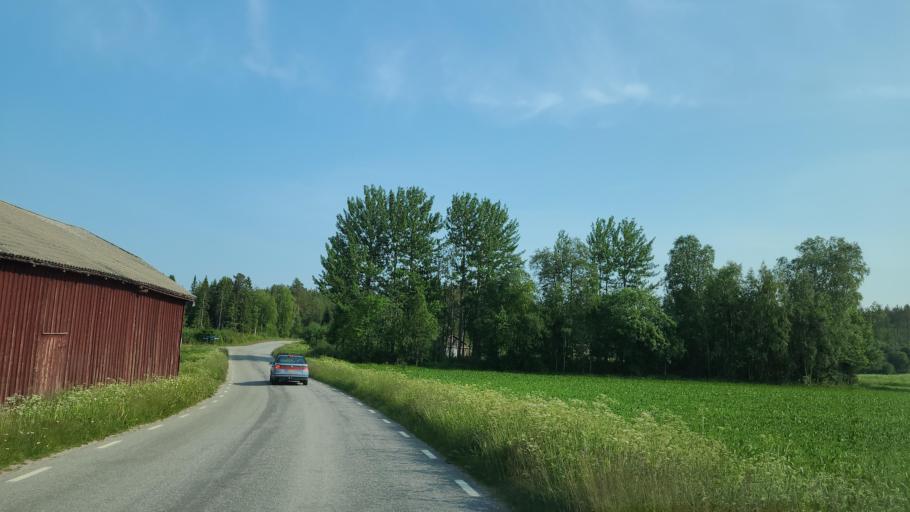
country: SE
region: Vaesterbotten
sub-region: Skelleftea Kommun
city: Burea
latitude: 64.3442
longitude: 21.3420
